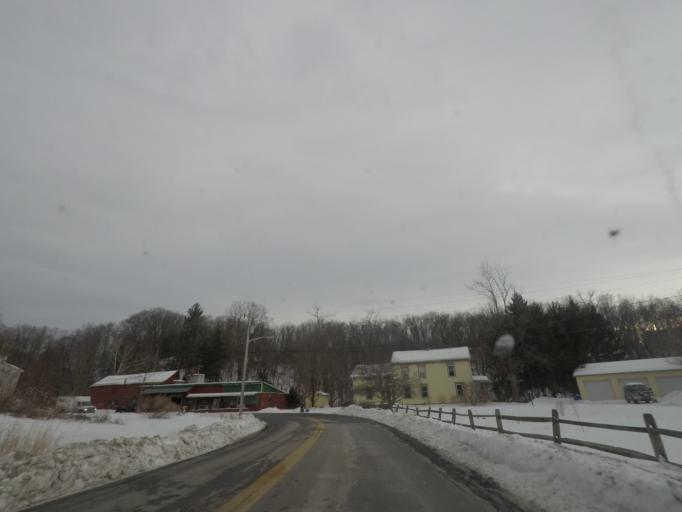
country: US
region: New York
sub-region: Rensselaer County
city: Castleton-on-Hudson
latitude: 42.5179
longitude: -73.7590
